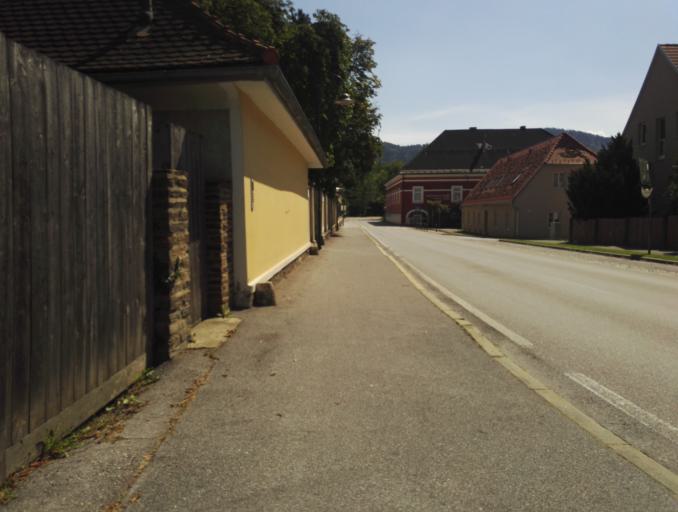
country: AT
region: Styria
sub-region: Politischer Bezirk Graz-Umgebung
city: Peggau
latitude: 47.2048
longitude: 15.3451
